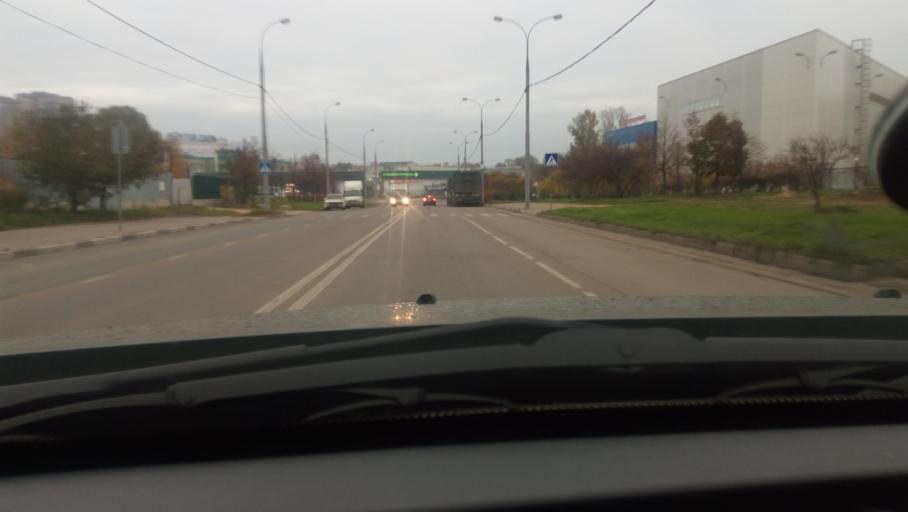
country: RU
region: Moskovskaya
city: Reutov
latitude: 55.7472
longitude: 37.8855
